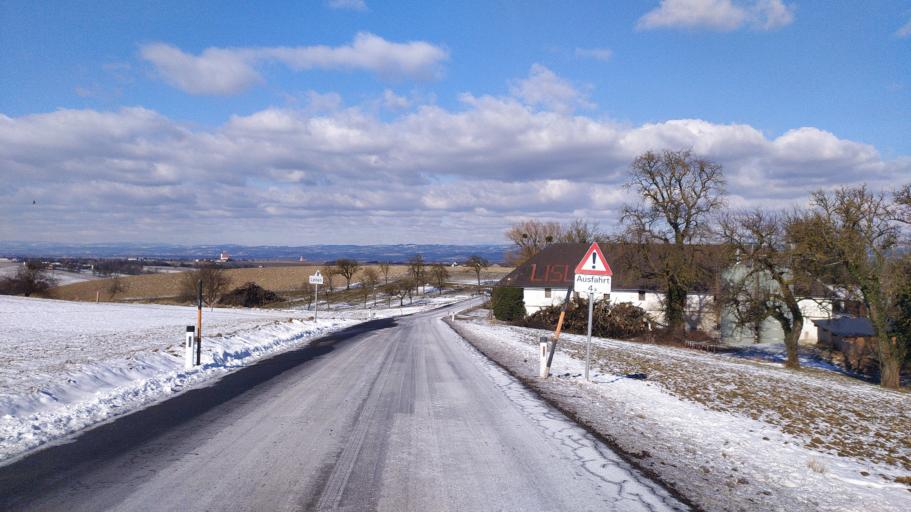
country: AT
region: Lower Austria
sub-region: Politischer Bezirk Amstetten
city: Zeillern
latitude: 48.1319
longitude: 14.7385
